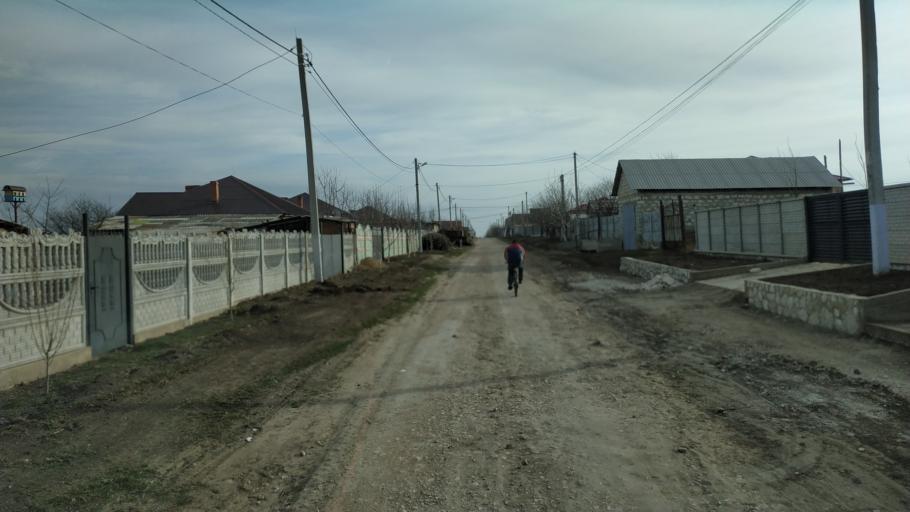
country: RO
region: Vaslui
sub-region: Comuna Dranceni
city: Dranceni
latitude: 46.8401
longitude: 28.1822
